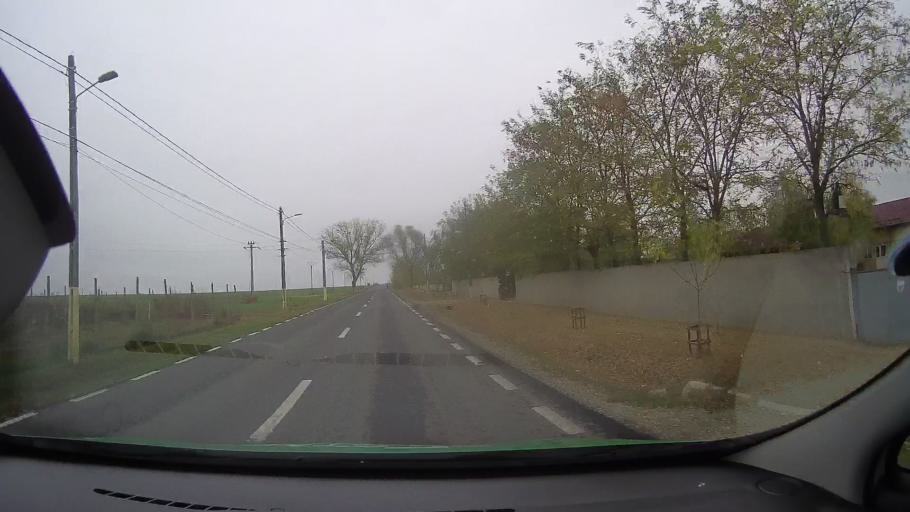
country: RO
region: Constanta
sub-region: Comuna Tortoman
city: Tortoman
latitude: 44.3495
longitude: 28.2178
